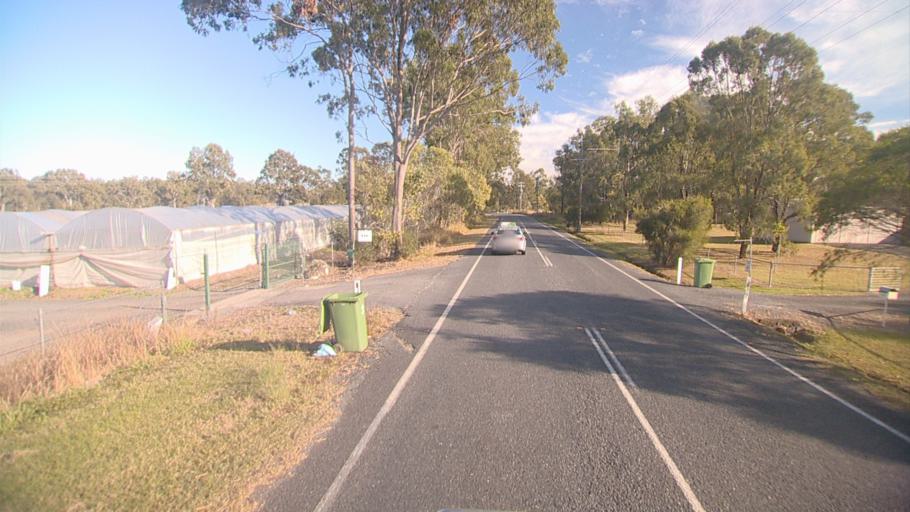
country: AU
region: Queensland
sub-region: Logan
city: North Maclean
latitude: -27.7535
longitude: 153.0014
